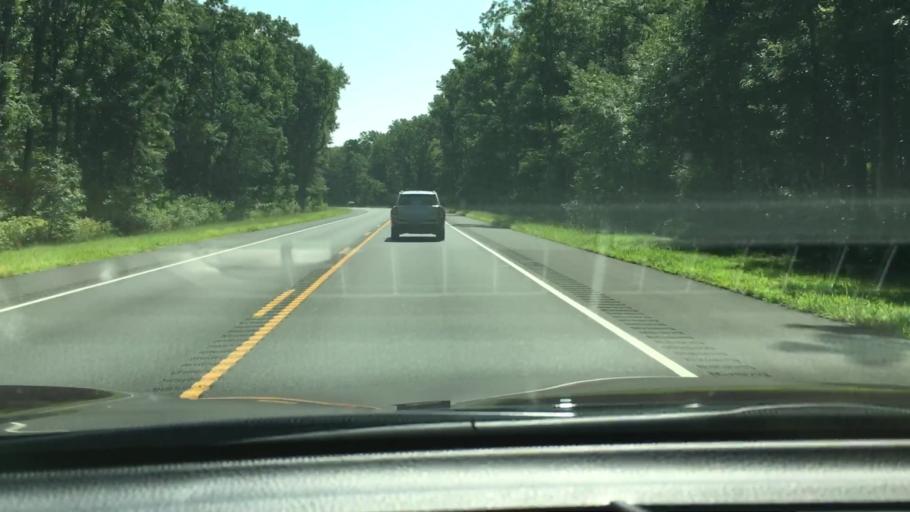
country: US
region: New Jersey
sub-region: Cape May County
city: Woodbine
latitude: 39.3183
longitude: -74.8476
